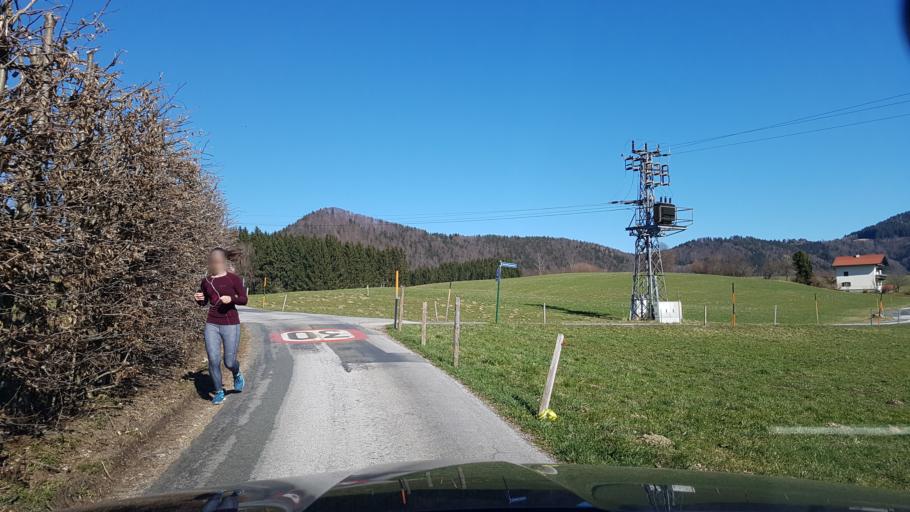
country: AT
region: Salzburg
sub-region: Politischer Bezirk Salzburg-Umgebung
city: Ebenau
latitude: 47.8063
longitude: 13.1758
